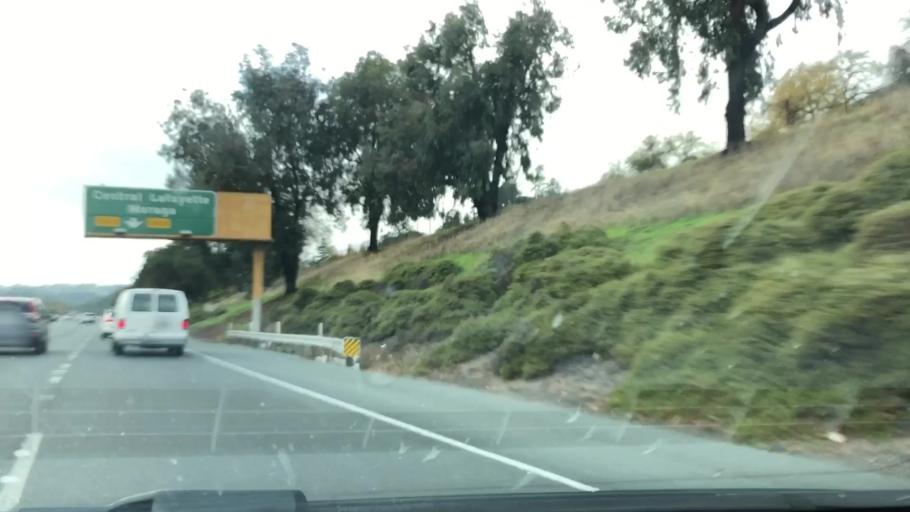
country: US
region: California
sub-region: Contra Costa County
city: Lafayette
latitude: 37.8972
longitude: -122.1028
